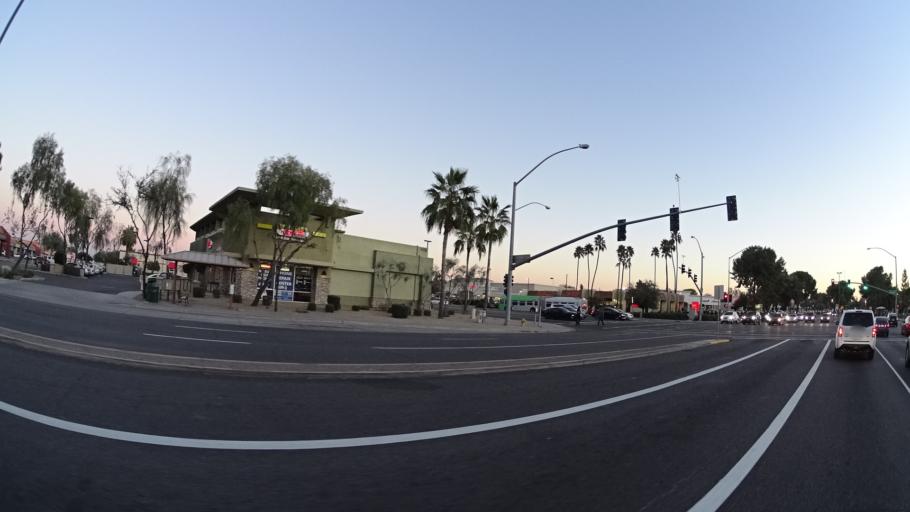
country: US
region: Arizona
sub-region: Maricopa County
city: San Carlos
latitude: 33.3790
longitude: -111.8778
